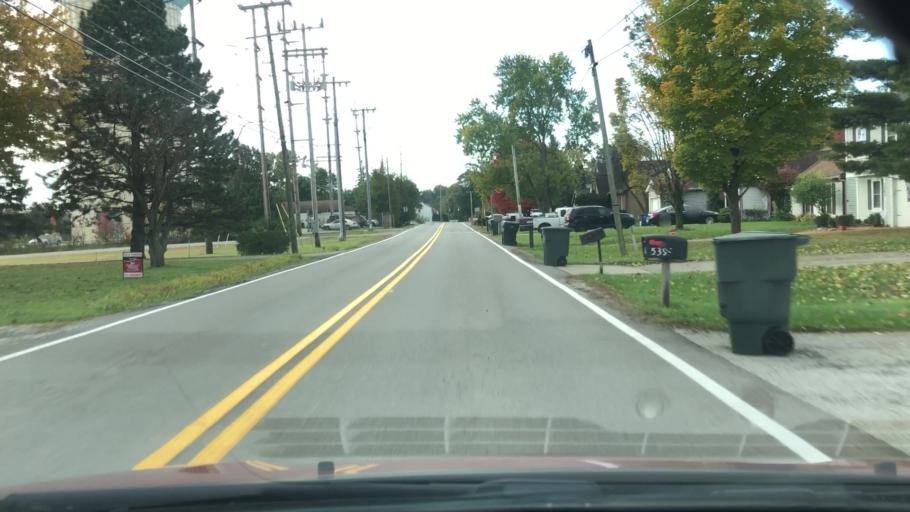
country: US
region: Ohio
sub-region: Franklin County
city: Huber Ridge
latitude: 40.0815
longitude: -82.8669
